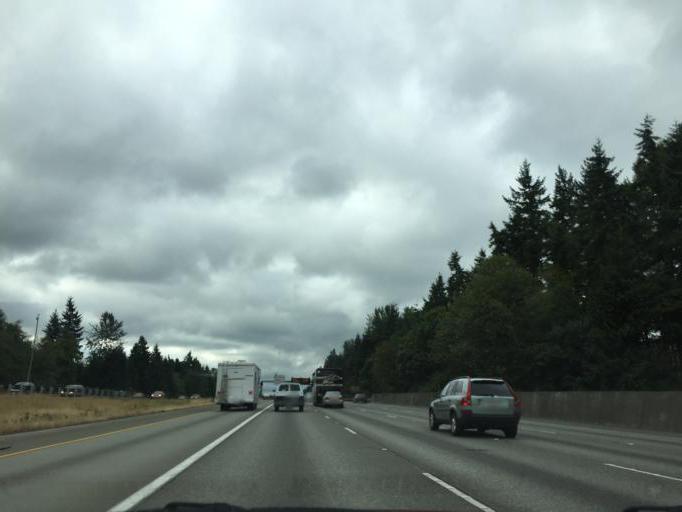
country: US
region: Washington
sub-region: King County
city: Lakeland North
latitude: 47.3371
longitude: -122.2935
